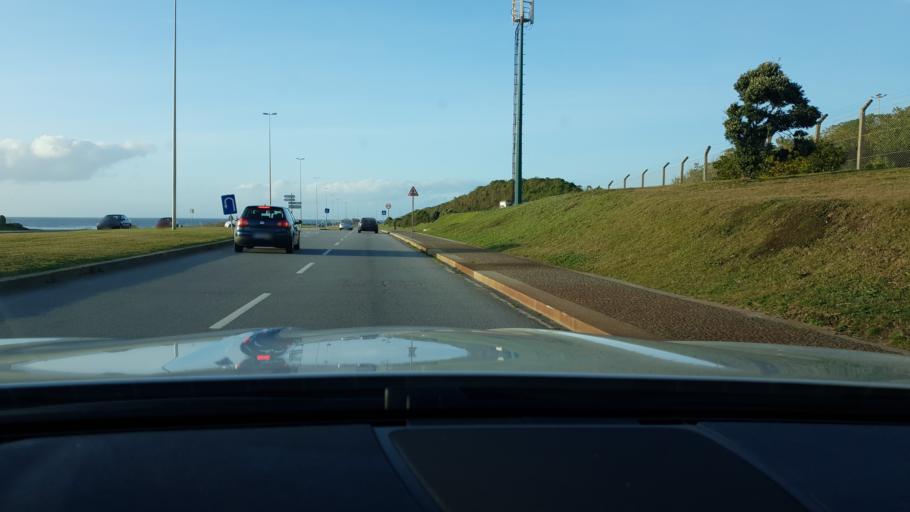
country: PT
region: Porto
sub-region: Matosinhos
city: Leca da Palmeira
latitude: 41.2021
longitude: -8.7115
